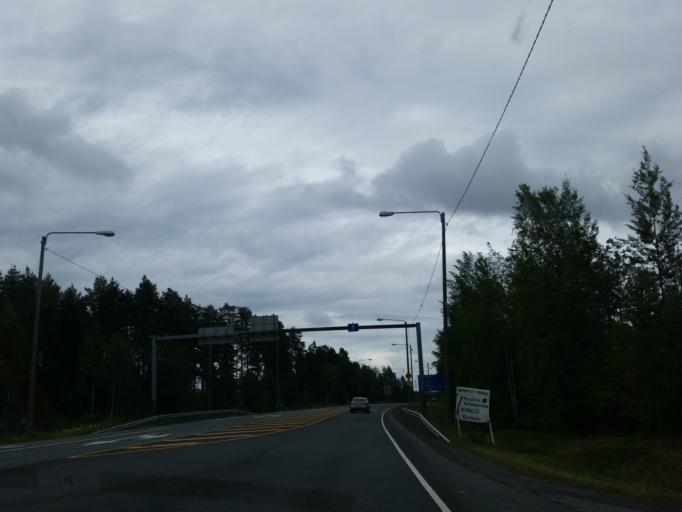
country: FI
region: Northern Savo
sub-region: Kuopio
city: Kuopio
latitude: 62.9819
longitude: 27.7242
